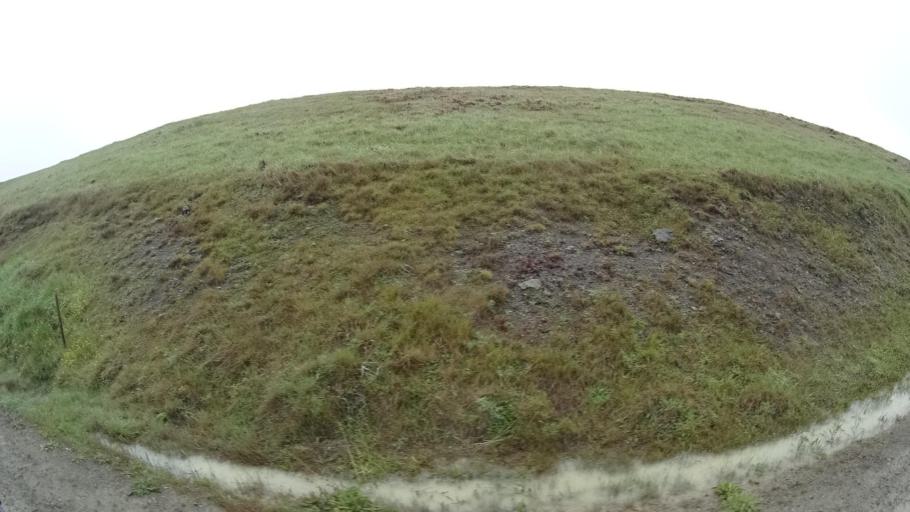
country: US
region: California
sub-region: Humboldt County
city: Westhaven-Moonstone
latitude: 41.1453
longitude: -123.8687
